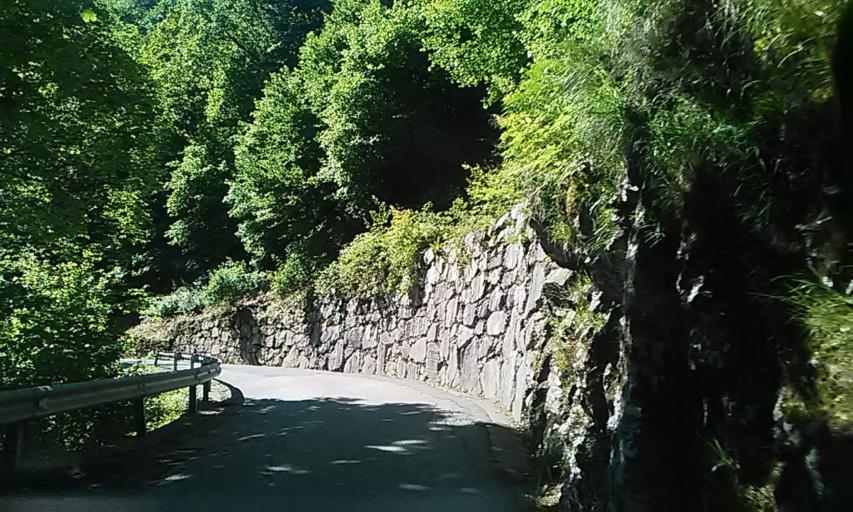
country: IT
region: Piedmont
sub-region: Provincia di Vercelli
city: Civiasco
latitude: 45.8422
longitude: 8.2839
